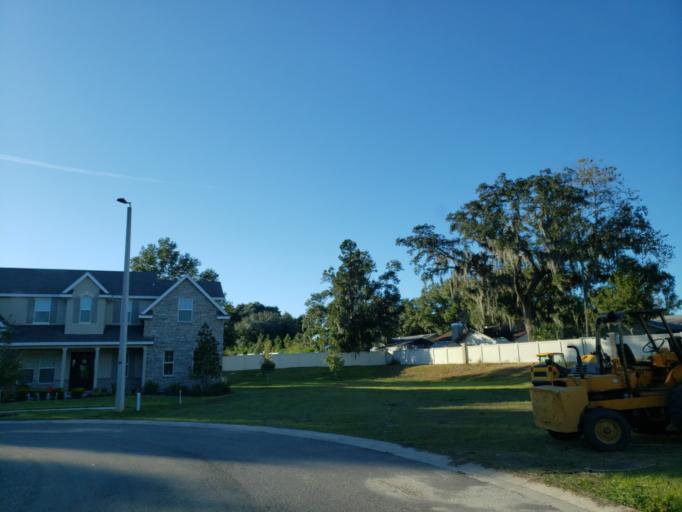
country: US
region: Florida
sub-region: Hillsborough County
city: Bloomingdale
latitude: 27.8971
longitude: -82.2396
